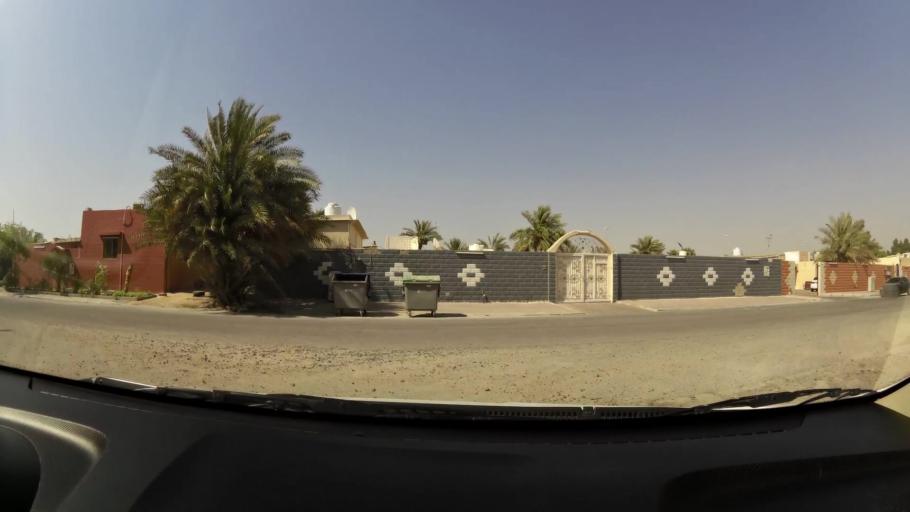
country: AE
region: Ajman
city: Ajman
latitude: 25.4132
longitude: 55.4739
